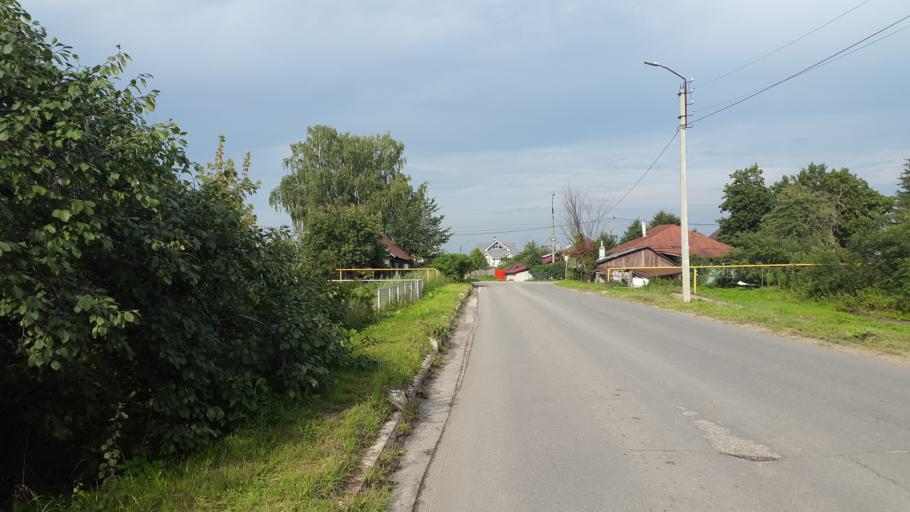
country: RU
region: Vladimir
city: Gorokhovets
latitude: 56.1973
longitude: 42.6919
